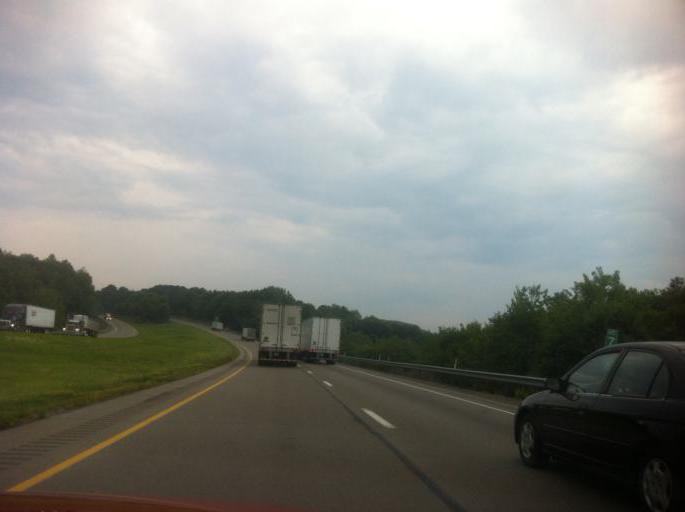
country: US
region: Pennsylvania
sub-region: Jefferson County
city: Brookville
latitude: 41.1876
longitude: -79.1728
